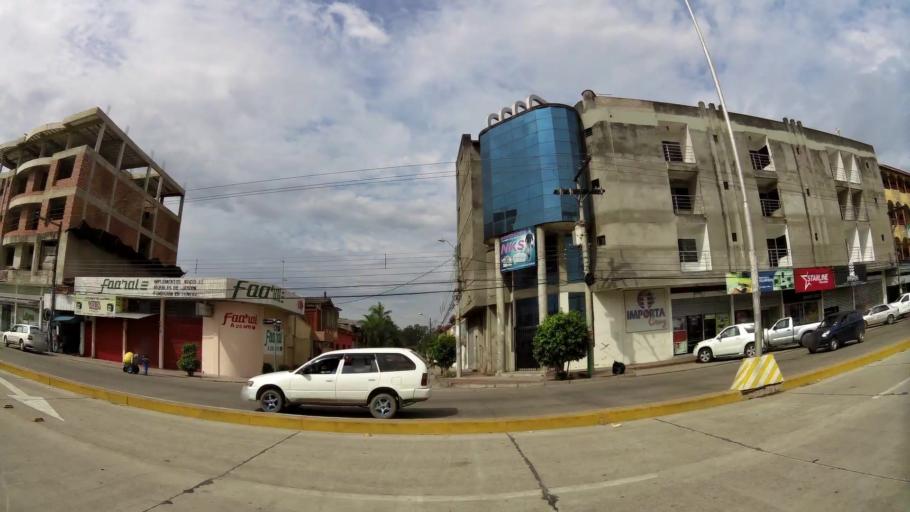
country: BO
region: Santa Cruz
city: Santa Cruz de la Sierra
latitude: -17.7815
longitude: -63.2043
